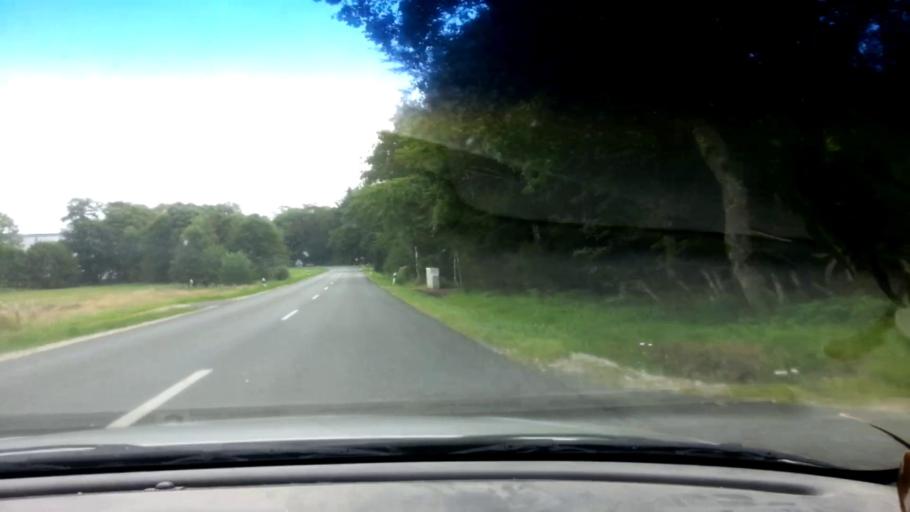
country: DE
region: Bavaria
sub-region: Upper Franconia
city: Grub
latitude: 50.0895
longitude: 11.9160
